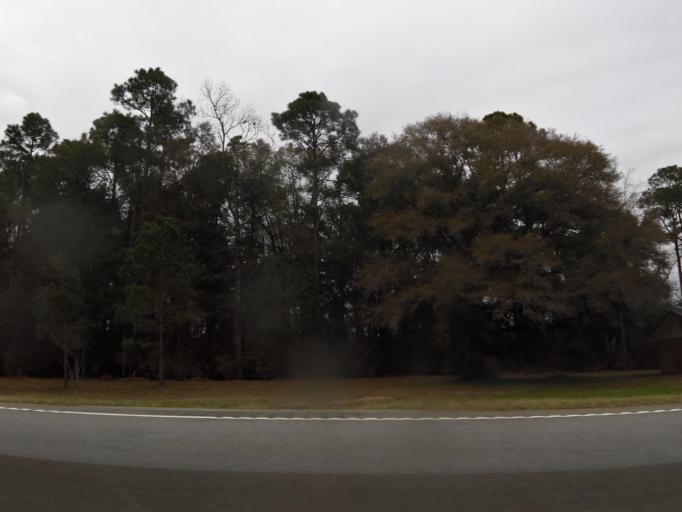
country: US
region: Georgia
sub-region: Randolph County
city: Shellman
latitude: 31.7824
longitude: -84.5951
